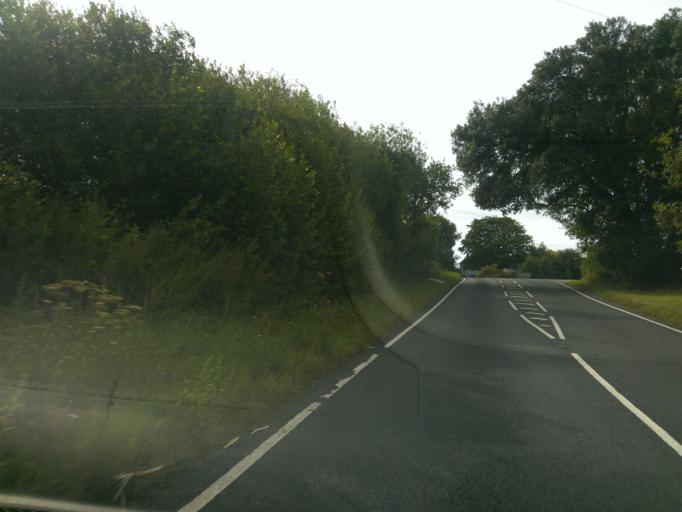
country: GB
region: England
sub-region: Essex
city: Saint Osyth
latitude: 51.8212
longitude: 1.0698
